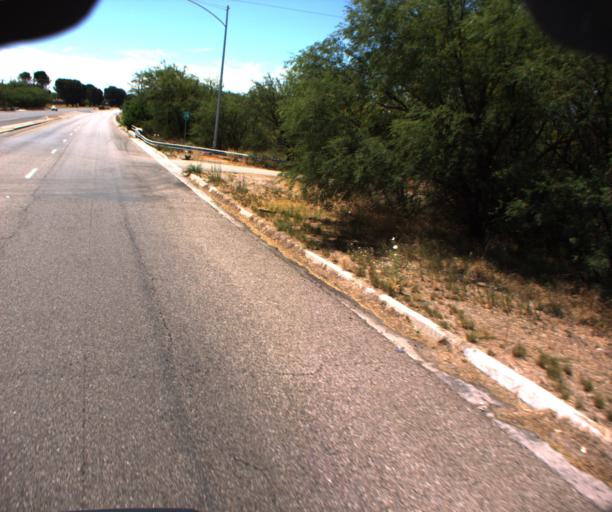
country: US
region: Arizona
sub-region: Santa Cruz County
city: Nogales
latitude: 31.3936
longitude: -110.9562
